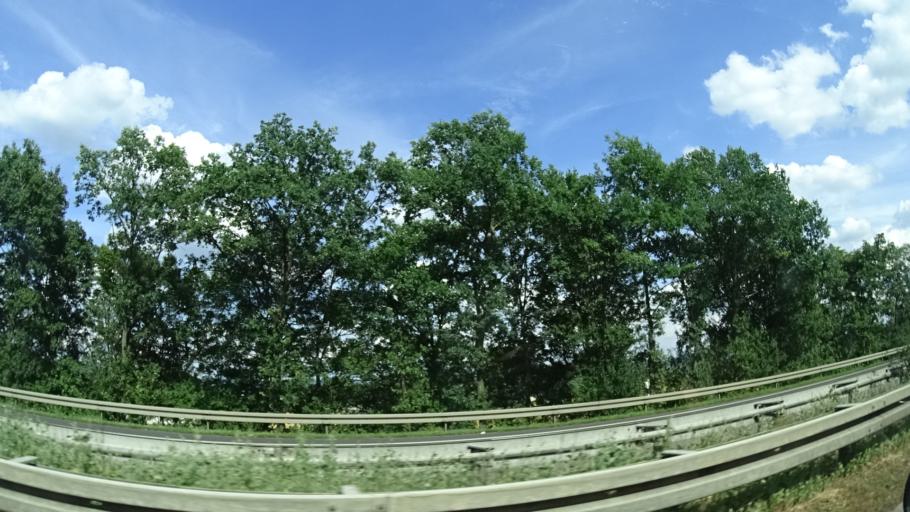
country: DE
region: Hesse
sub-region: Regierungsbezirk Kassel
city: Petersberg
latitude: 50.5610
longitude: 9.7293
